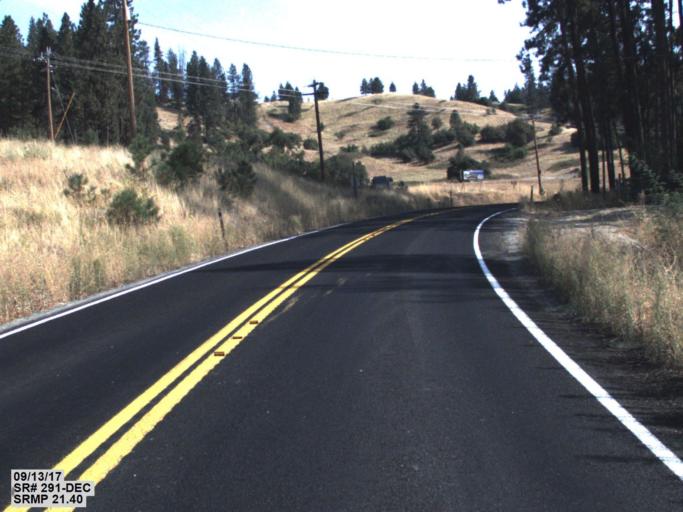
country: US
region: Washington
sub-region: Spokane County
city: Deer Park
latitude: 47.8939
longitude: -117.6692
